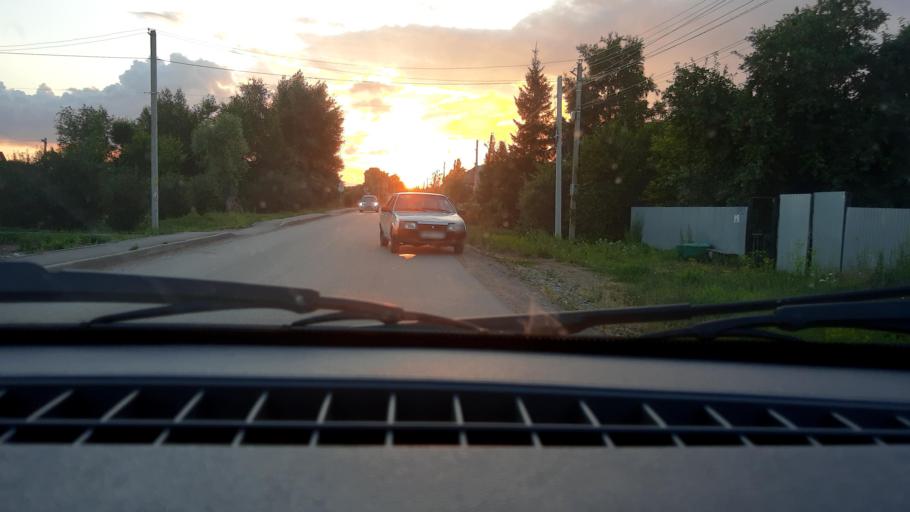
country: RU
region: Bashkortostan
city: Mikhaylovka
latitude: 54.7852
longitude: 55.8148
